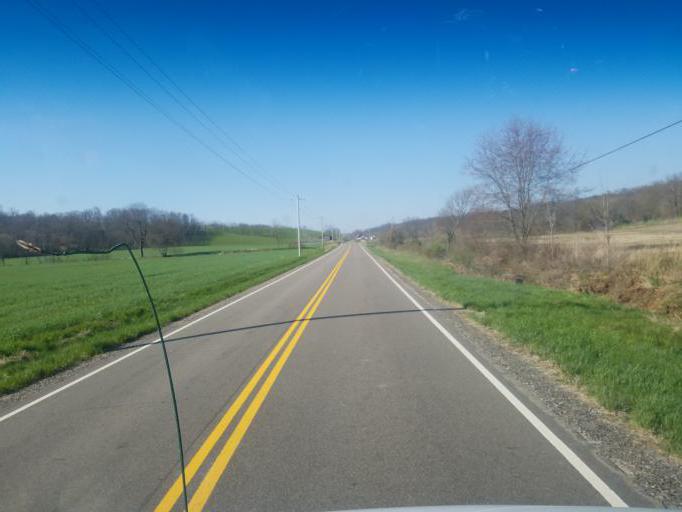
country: US
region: Ohio
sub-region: Muskingum County
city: Frazeysburg
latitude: 40.2868
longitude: -82.0904
